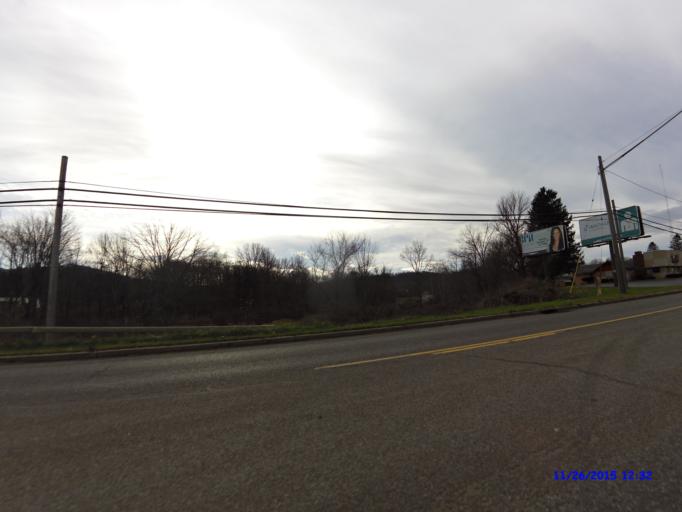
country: US
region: New York
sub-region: Cattaraugus County
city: Saint Bonaventure
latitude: 42.0769
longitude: -78.4695
